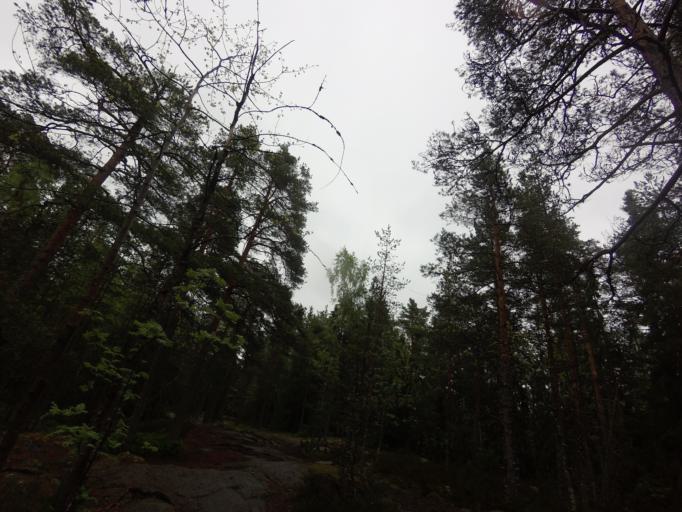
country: FI
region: Uusimaa
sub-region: Helsinki
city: Kauniainen
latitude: 60.1866
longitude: 24.7036
